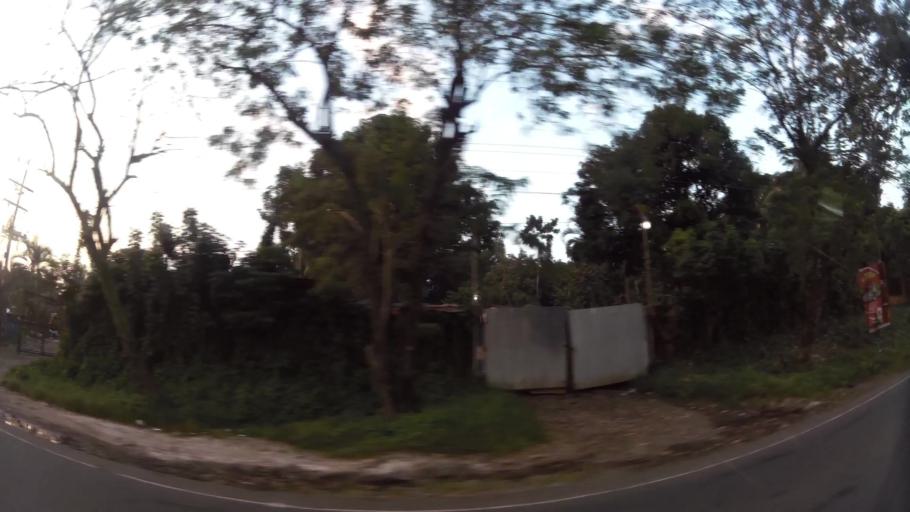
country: GT
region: Retalhuleu
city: Santa Cruz Mulua
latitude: 14.5843
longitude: -91.6245
